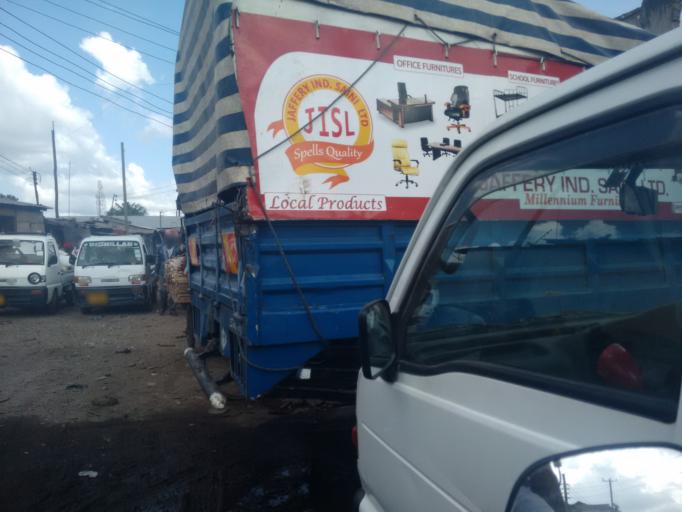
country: TZ
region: Dar es Salaam
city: Dar es Salaam
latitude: -6.8372
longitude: 39.2709
